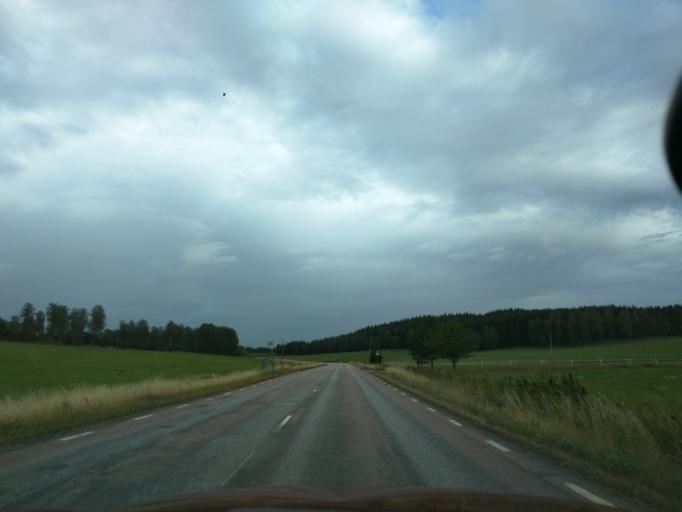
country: SE
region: Soedermanland
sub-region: Oxelosunds Kommun
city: Oxelosund
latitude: 58.8580
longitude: 17.1937
